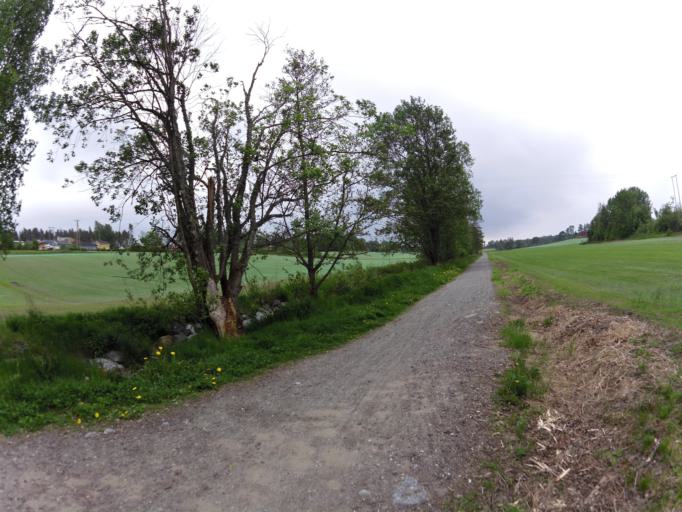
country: NO
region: Ostfold
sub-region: Rygge
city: Larkollen
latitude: 59.3839
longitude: 10.6861
